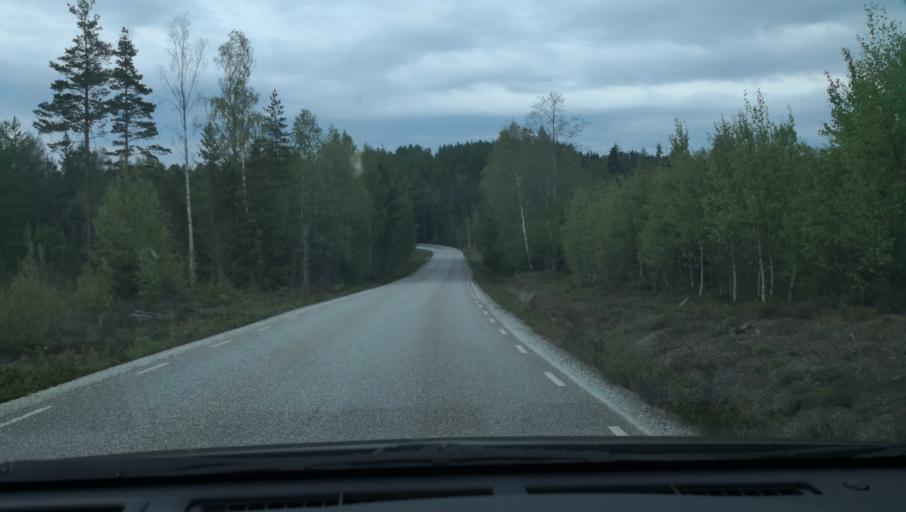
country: SE
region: Vaestmanland
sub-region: Skinnskattebergs Kommun
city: Skinnskatteberg
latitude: 59.8301
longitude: 15.5770
